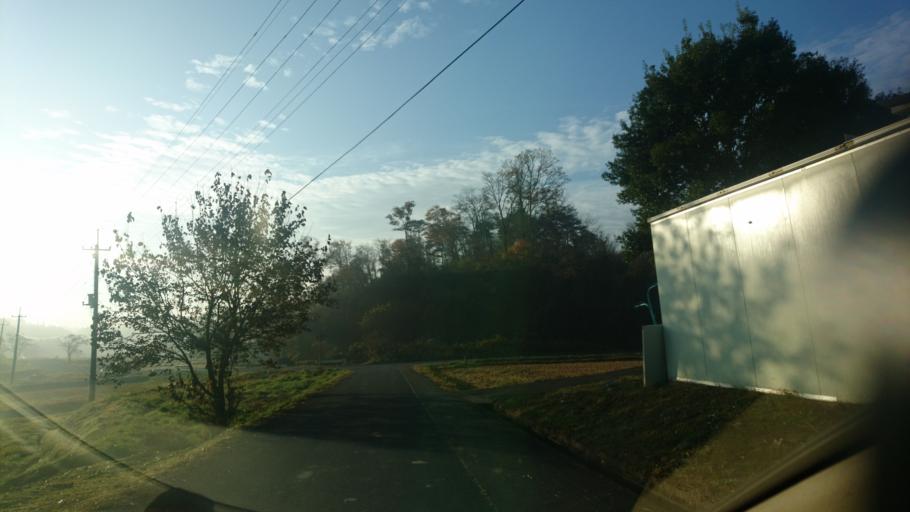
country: JP
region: Iwate
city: Ichinoseki
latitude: 38.9286
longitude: 141.2061
